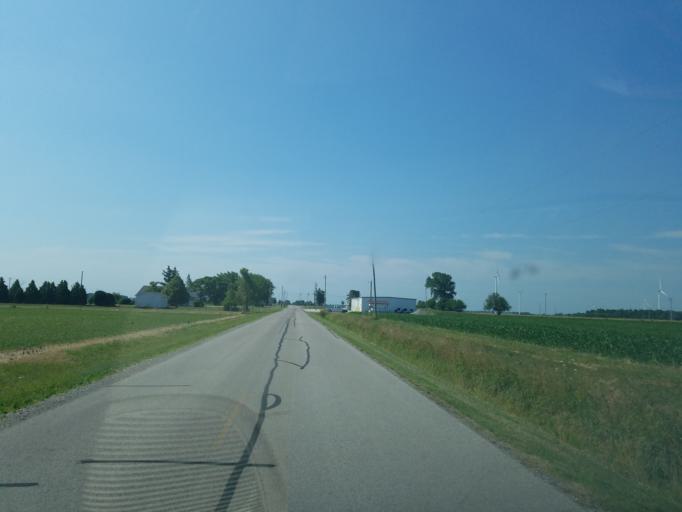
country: US
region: Ohio
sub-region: Van Wert County
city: Convoy
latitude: 40.9478
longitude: -84.6299
